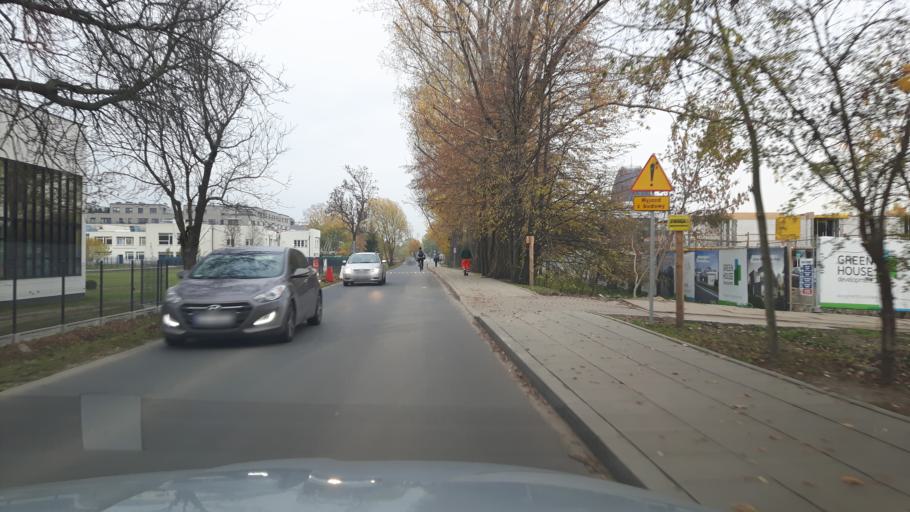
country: PL
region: Masovian Voivodeship
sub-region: Warszawa
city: Ursynow
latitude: 52.1571
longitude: 21.0643
